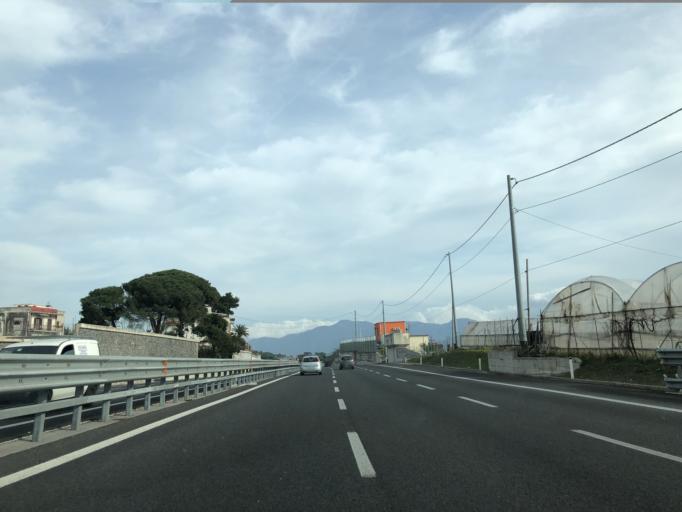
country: IT
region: Campania
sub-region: Provincia di Napoli
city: Torre del Greco
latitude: 40.7789
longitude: 14.3951
